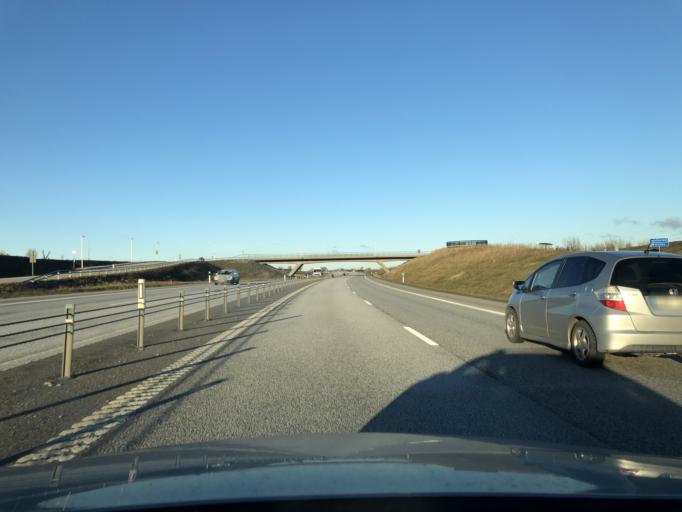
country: SE
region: Skane
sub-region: Trelleborgs Kommun
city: Skare
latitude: 55.4065
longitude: 13.0632
